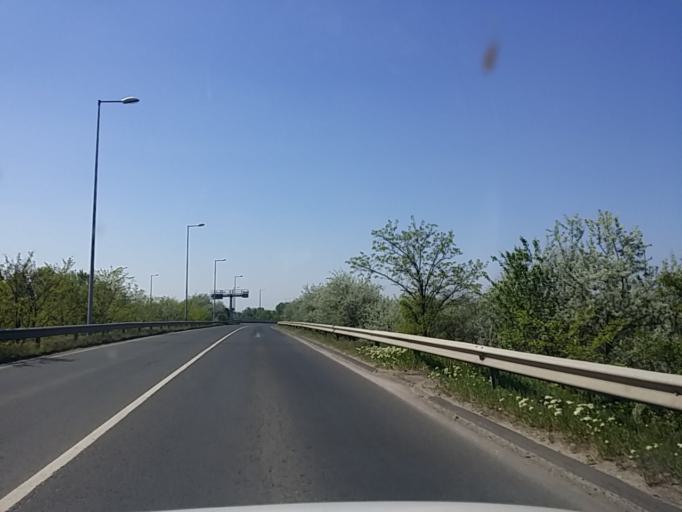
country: HU
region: Budapest
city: Budapest XV. keruelet
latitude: 47.5823
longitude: 19.1510
